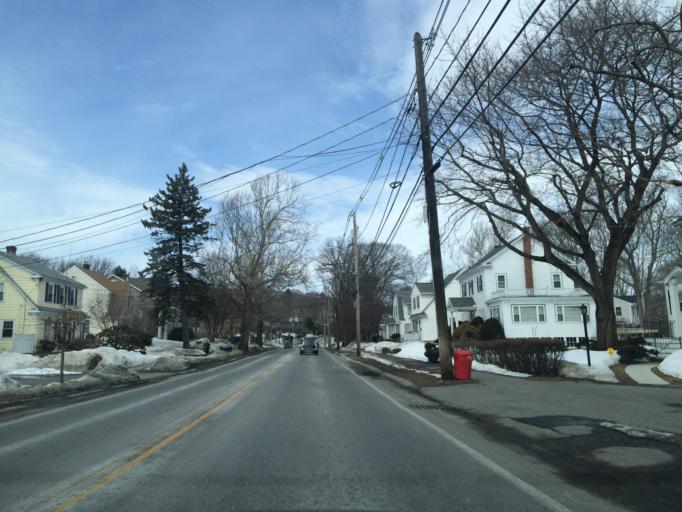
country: US
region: Massachusetts
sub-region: Middlesex County
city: Lexington
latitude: 42.4334
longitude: -71.2340
